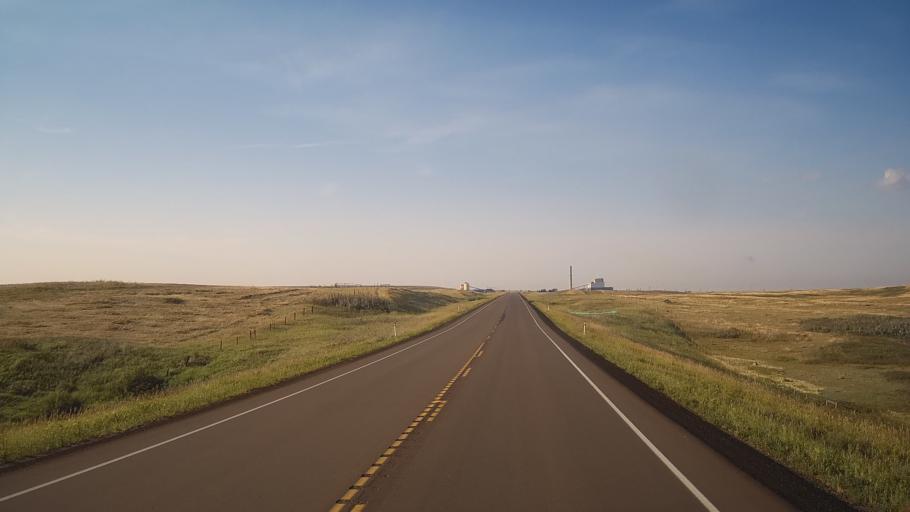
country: CA
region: Alberta
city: Hanna
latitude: 51.4761
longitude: -111.7864
